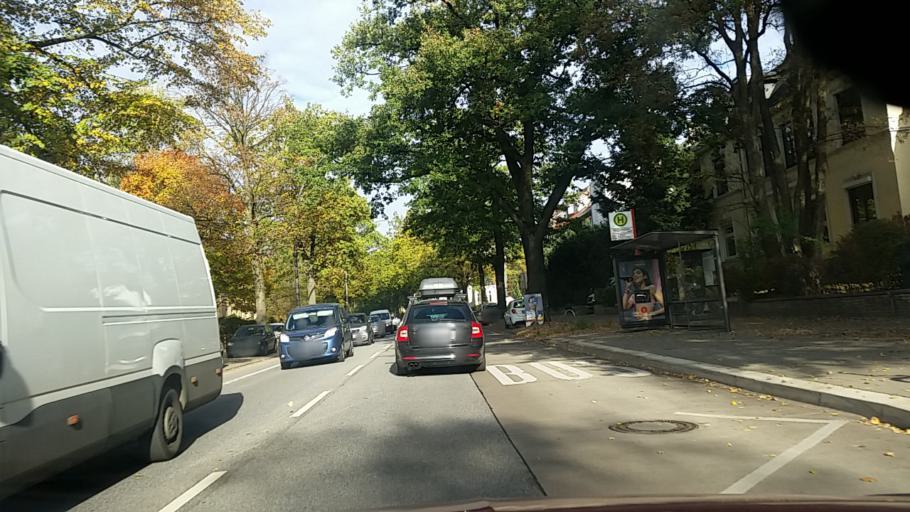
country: DE
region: Hamburg
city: Barmbek-Nord
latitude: 53.6120
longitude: 10.0369
